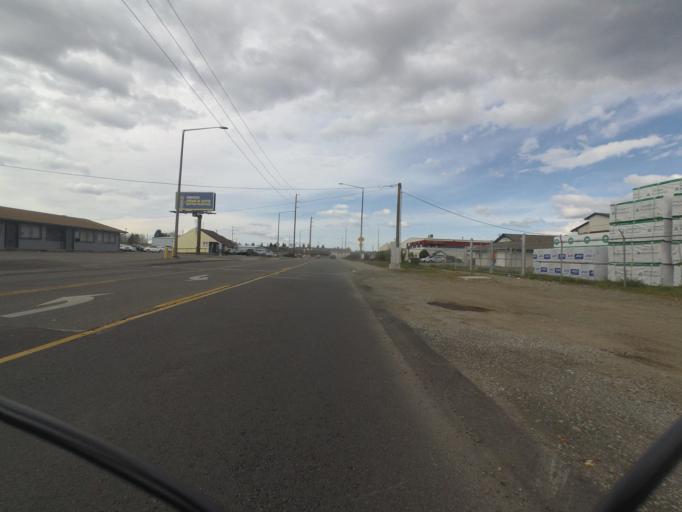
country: US
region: Washington
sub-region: Pierce County
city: Lakewood
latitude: 47.1682
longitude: -122.4907
